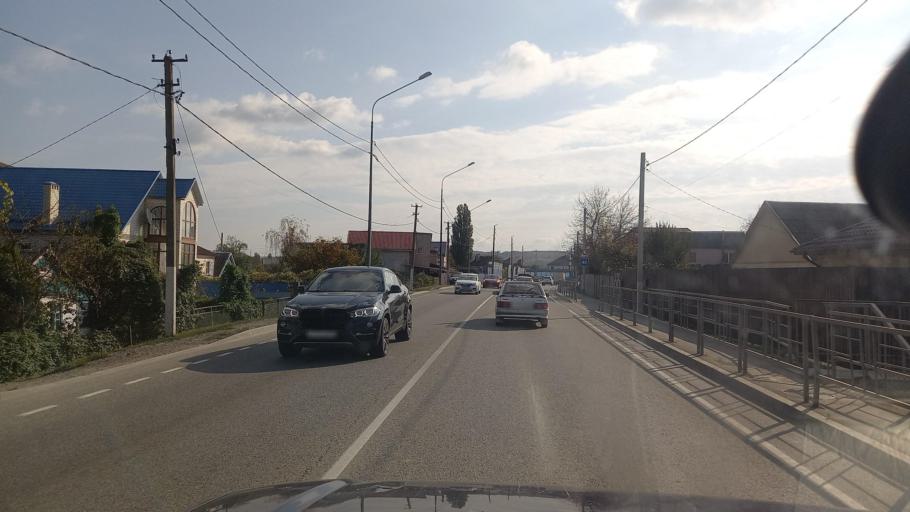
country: RU
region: Krasnodarskiy
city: Krymsk
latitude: 44.8683
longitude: 37.8512
